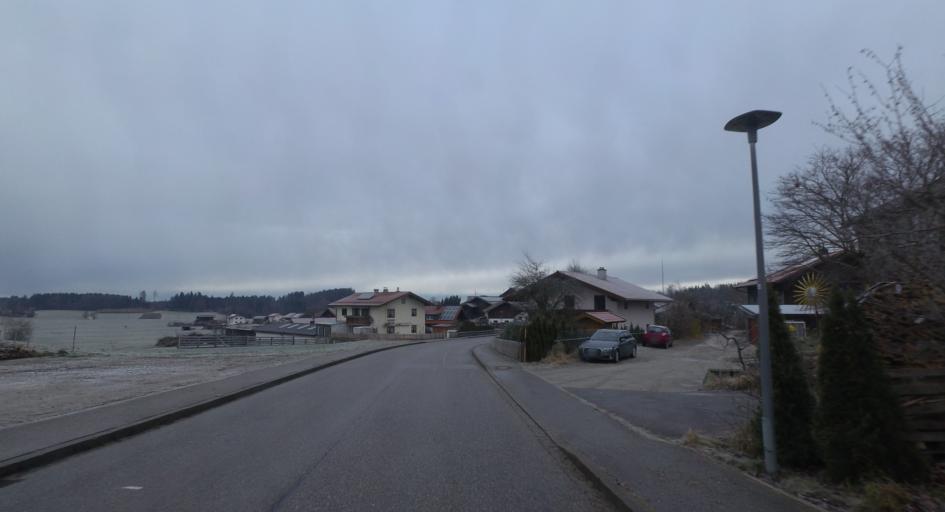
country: DE
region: Bavaria
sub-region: Upper Bavaria
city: Traunstein
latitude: 47.9112
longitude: 12.6500
